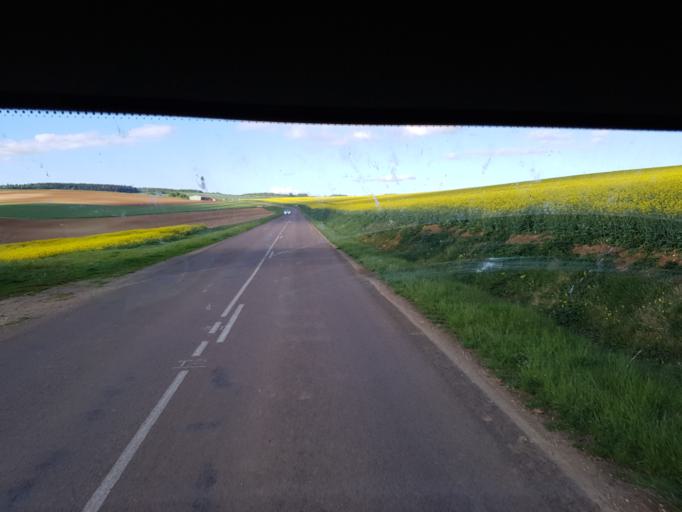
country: FR
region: Champagne-Ardenne
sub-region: Departement de l'Aube
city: Aix-en-Othe
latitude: 48.2592
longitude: 3.6453
